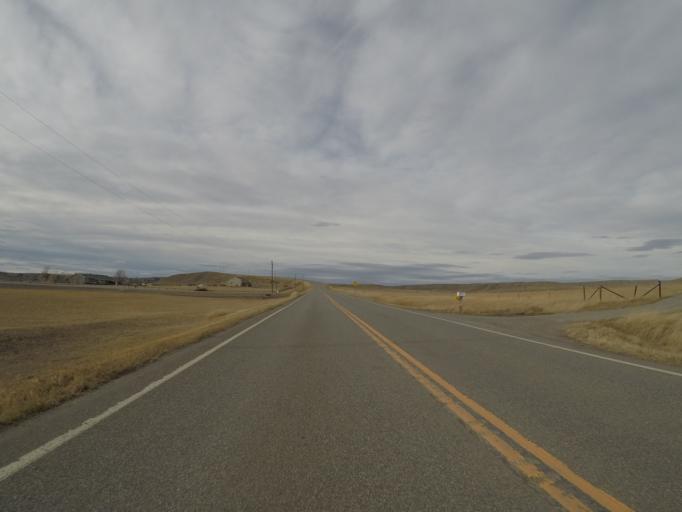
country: US
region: Montana
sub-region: Yellowstone County
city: Laurel
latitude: 45.8430
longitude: -108.7250
